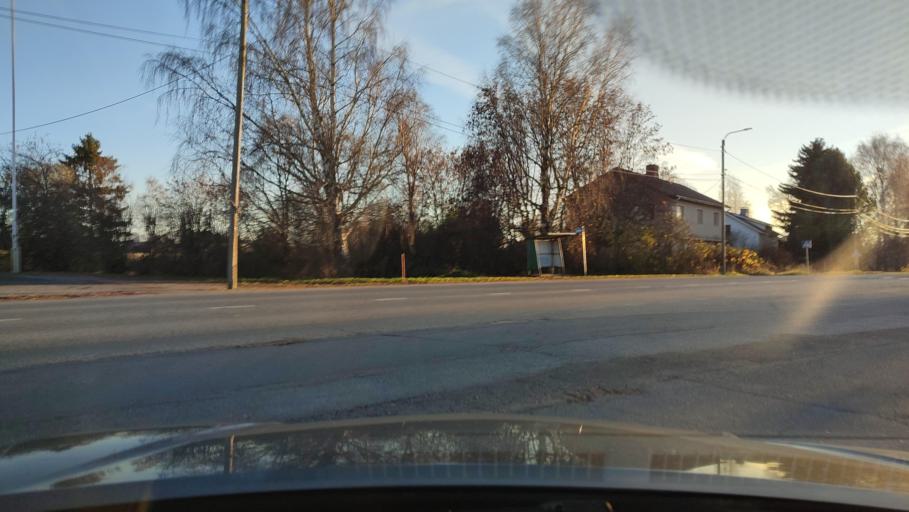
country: FI
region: Ostrobothnia
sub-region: Sydosterbotten
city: Naerpes
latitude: 62.6110
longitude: 21.4701
